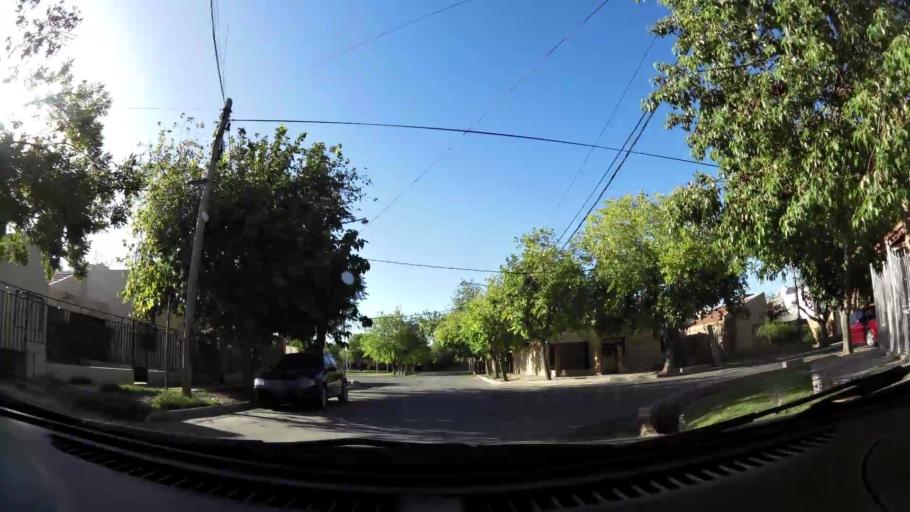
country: AR
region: San Juan
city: Villa Krause
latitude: -31.5612
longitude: -68.5162
